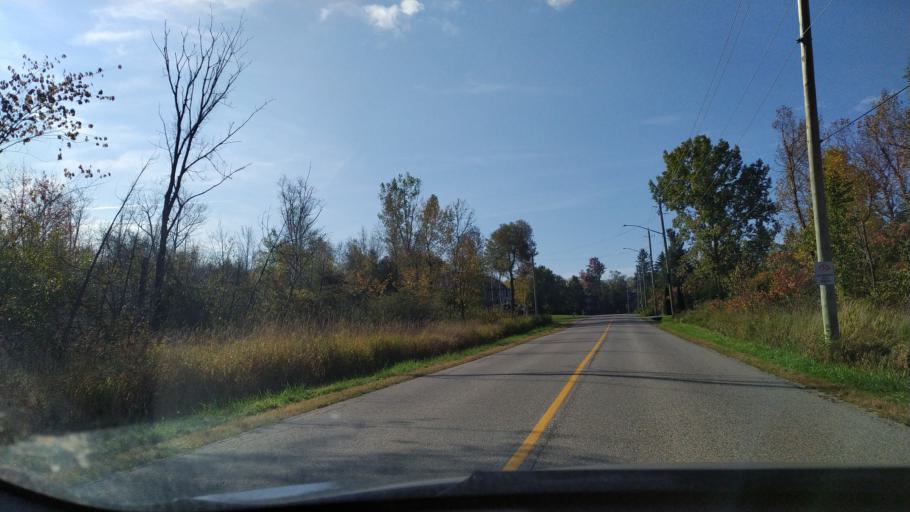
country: CA
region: Ontario
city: Waterloo
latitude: 43.5010
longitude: -80.6557
